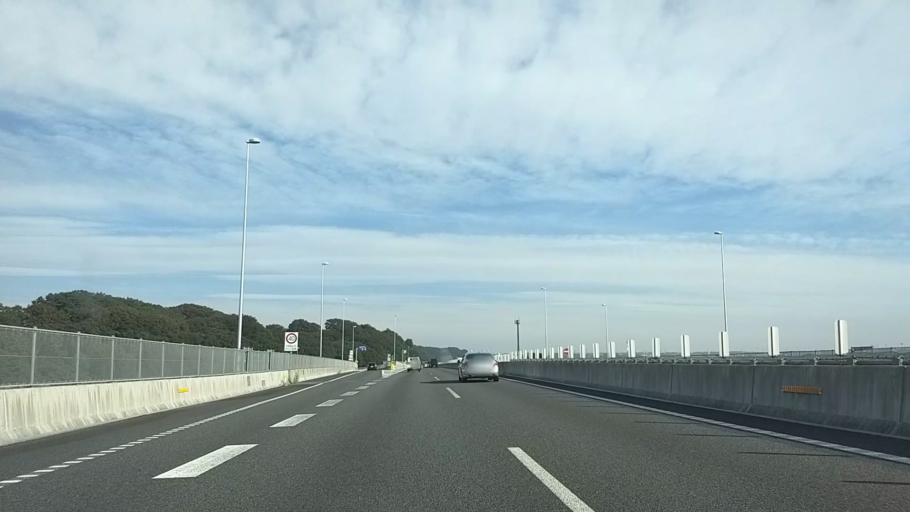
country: JP
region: Kanagawa
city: Zama
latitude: 35.4871
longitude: 139.3702
